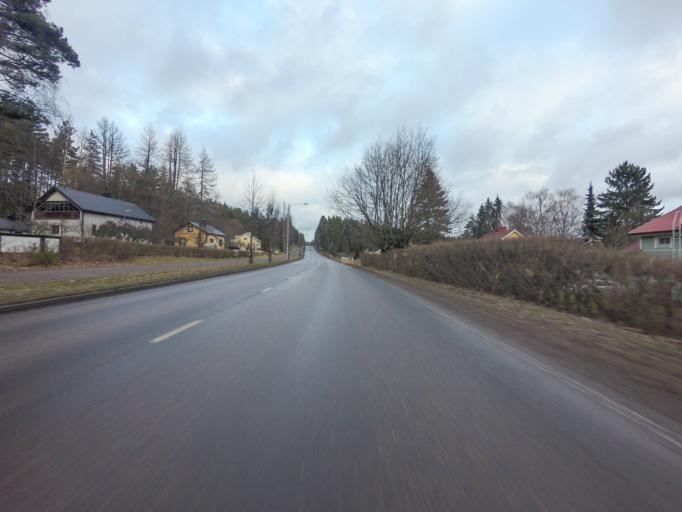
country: FI
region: Uusimaa
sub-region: Helsinki
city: Lohja
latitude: 60.2687
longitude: 24.1249
